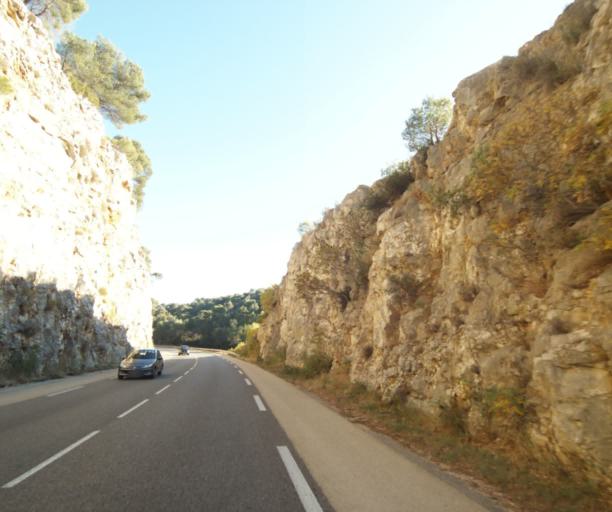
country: FR
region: Provence-Alpes-Cote d'Azur
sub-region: Departement des Bouches-du-Rhone
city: Cassis
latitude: 43.2082
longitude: 5.5811
